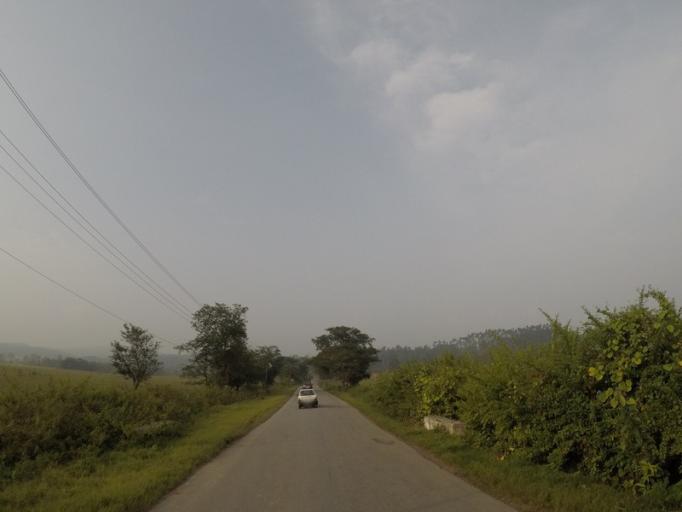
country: IN
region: Karnataka
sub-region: Chikmagalur
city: Mudigere
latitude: 13.2512
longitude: 75.6613
